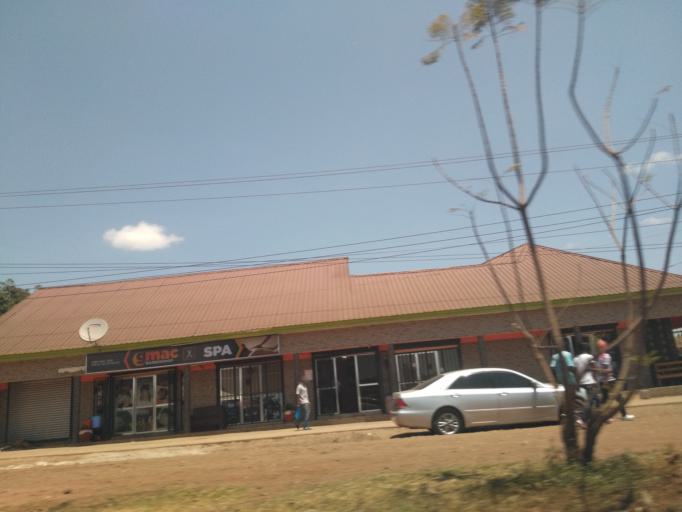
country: TZ
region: Arusha
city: Arusha
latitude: -3.3695
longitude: 36.6757
